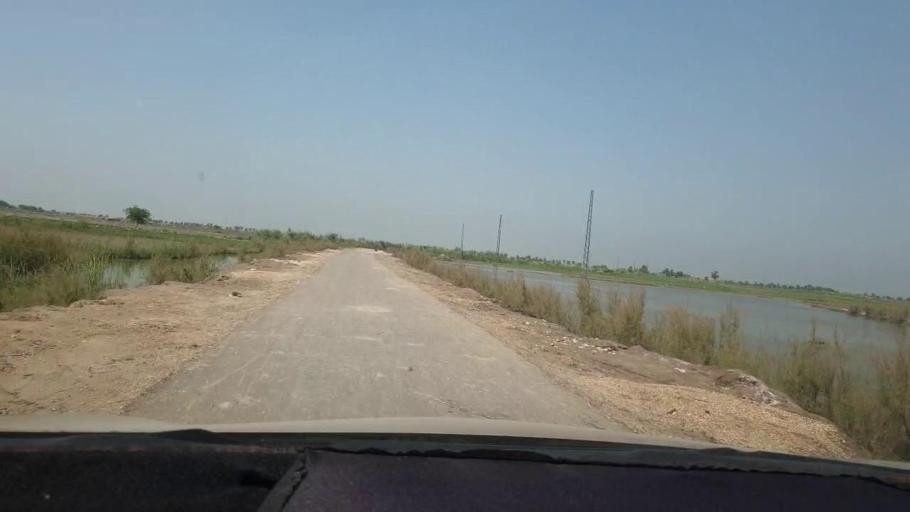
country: PK
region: Sindh
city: Shahdadkot
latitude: 27.8344
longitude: 67.8783
